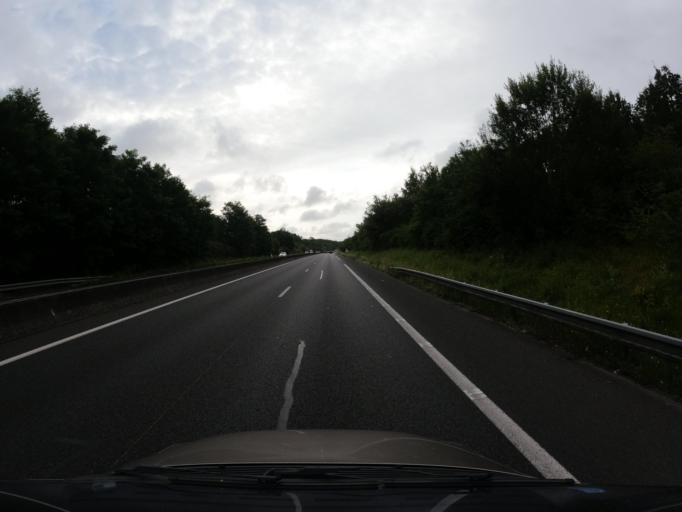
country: FR
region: Centre
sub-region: Departement d'Indre-et-Loire
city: Villandry
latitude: 47.3235
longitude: 0.4863
